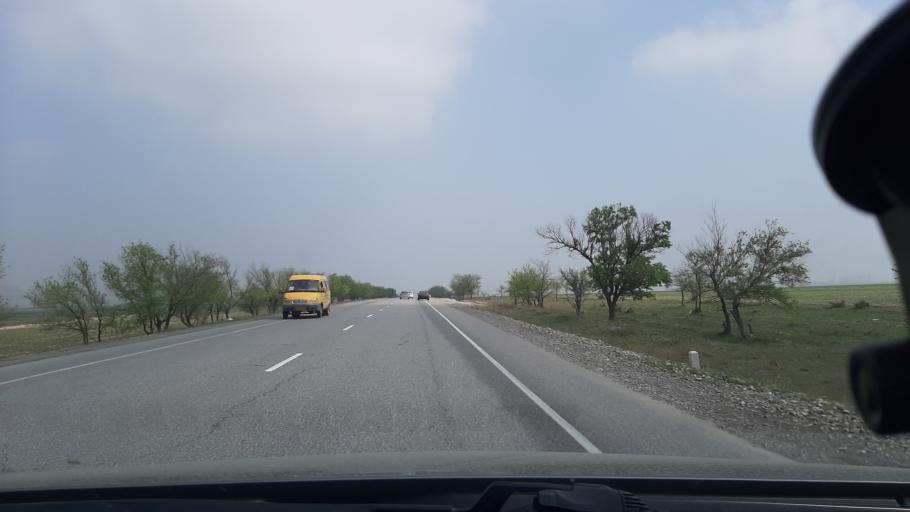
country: UZ
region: Toshkent
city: Bekobod
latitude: 40.1101
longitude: 69.1904
